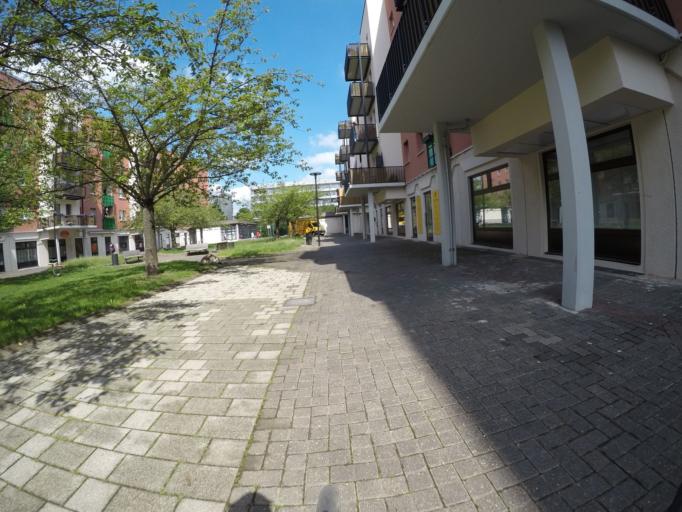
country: DE
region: Berlin
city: Hellersdorf
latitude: 52.5420
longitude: 13.6066
